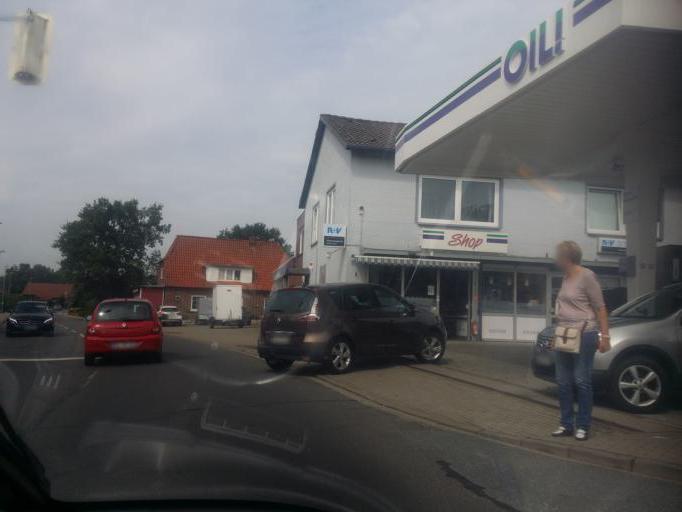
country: DE
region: Schleswig-Holstein
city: Sankt Michaelisdonn
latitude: 53.9885
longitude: 9.1140
